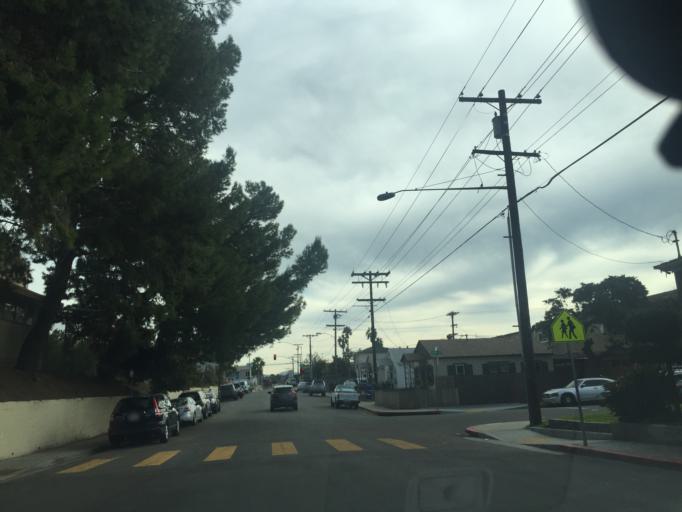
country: US
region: California
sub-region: San Diego County
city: Lemon Grove
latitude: 32.7514
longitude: -117.0937
